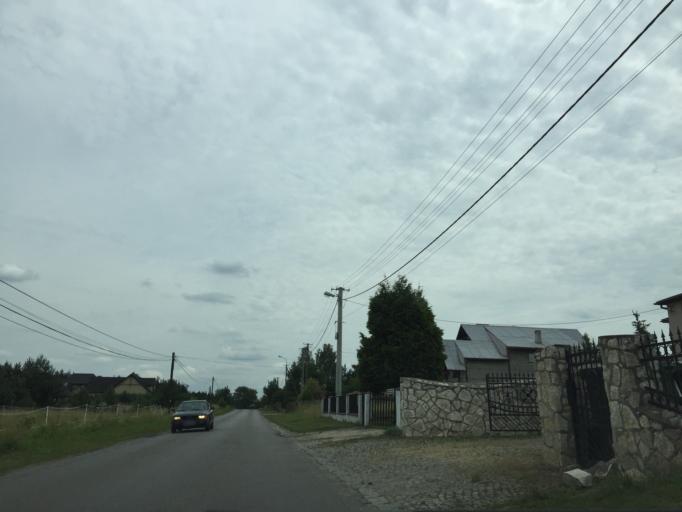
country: PL
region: Lesser Poland Voivodeship
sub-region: Powiat olkuski
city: Klucze
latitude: 50.3658
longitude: 19.5393
